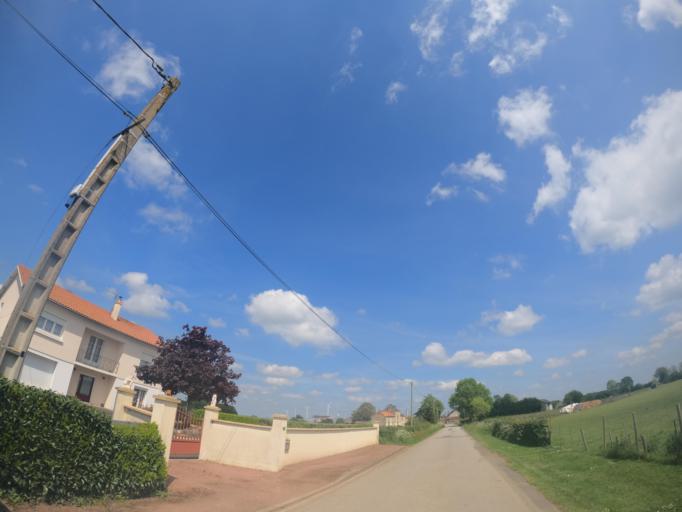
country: FR
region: Poitou-Charentes
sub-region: Departement des Deux-Sevres
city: Saint-Varent
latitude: 46.8457
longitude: -0.2271
